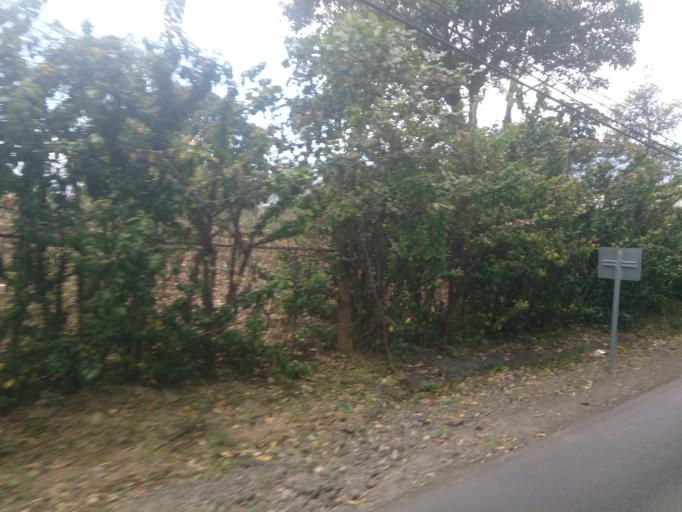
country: CR
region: San Jose
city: Granadilla
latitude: 9.9269
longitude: -84.0185
